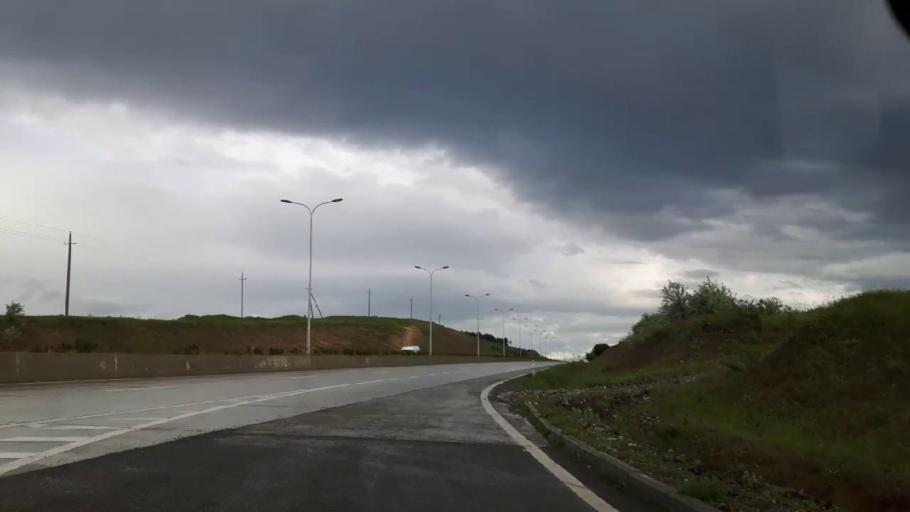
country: GE
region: Shida Kartli
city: Gori
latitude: 42.0129
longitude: 44.0354
